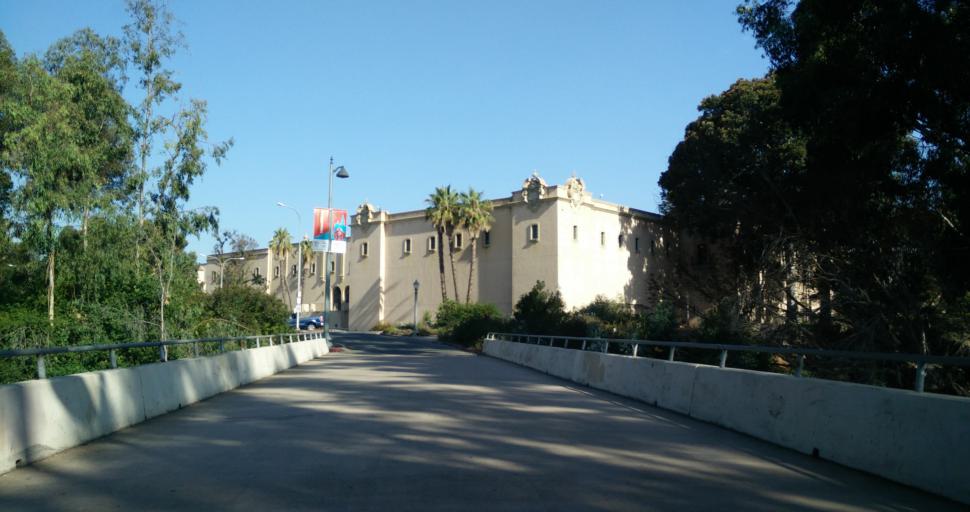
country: US
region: California
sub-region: San Diego County
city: San Diego
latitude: 32.7302
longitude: -117.1477
